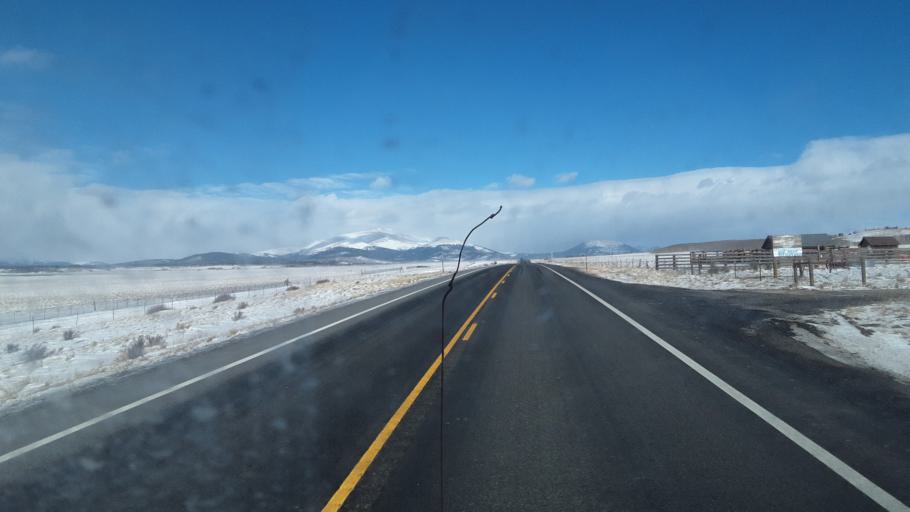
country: US
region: Colorado
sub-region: Park County
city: Fairplay
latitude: 39.1765
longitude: -106.0003
